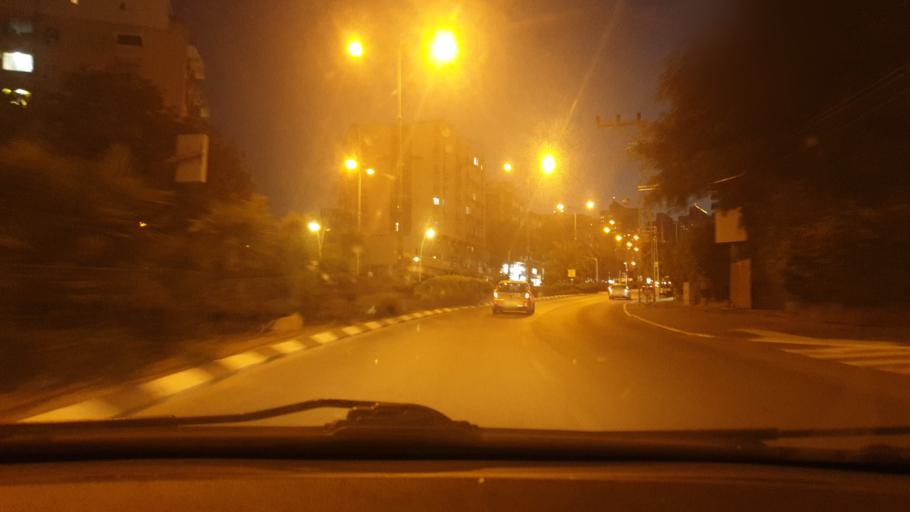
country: IL
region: Central District
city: Rishon LeZiyyon
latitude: 31.9716
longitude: 34.8062
